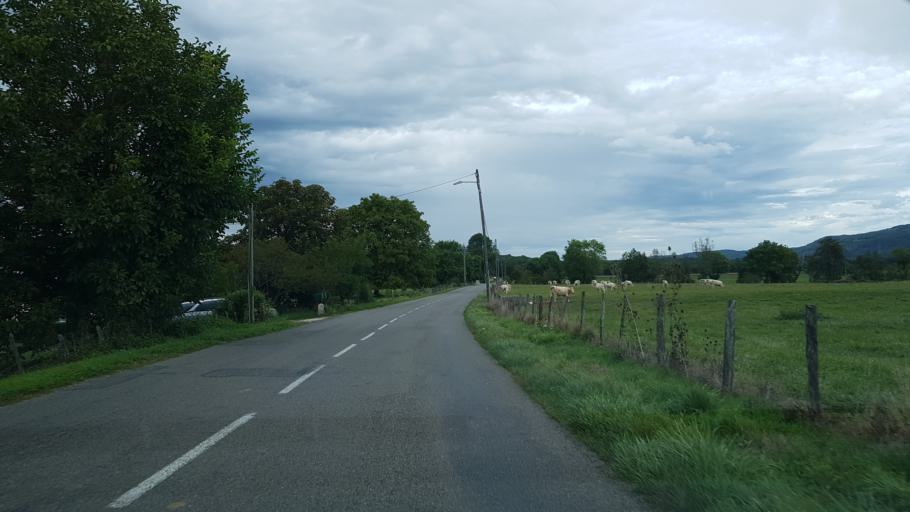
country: FR
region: Rhone-Alpes
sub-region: Departement de l'Ain
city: Villereversure
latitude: 46.1985
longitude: 5.3978
